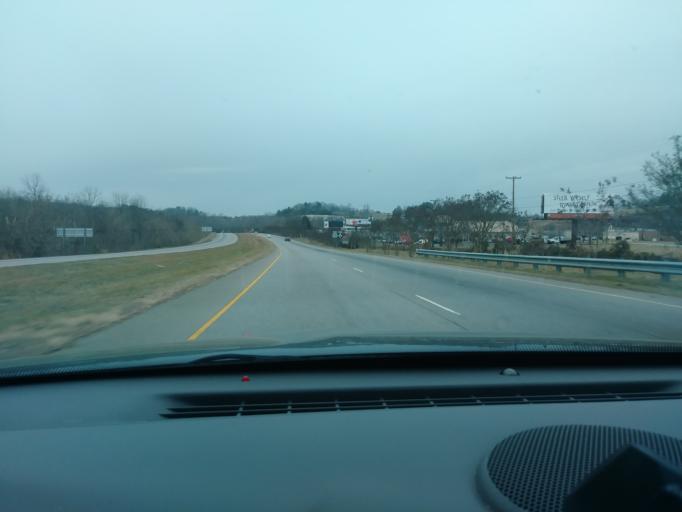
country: US
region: North Carolina
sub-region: Wilkes County
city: Wilkesboro
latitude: 36.1460
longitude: -81.1782
